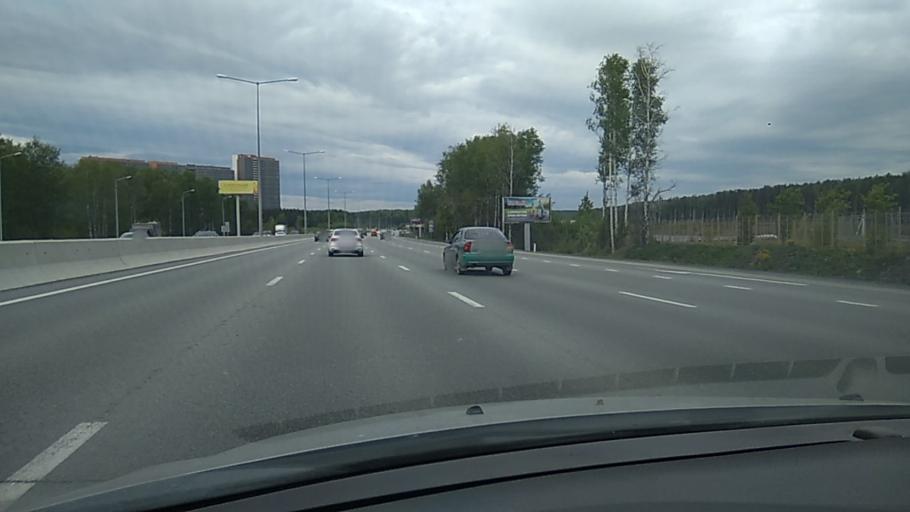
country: RU
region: Sverdlovsk
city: Istok
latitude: 56.7747
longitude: 60.7167
